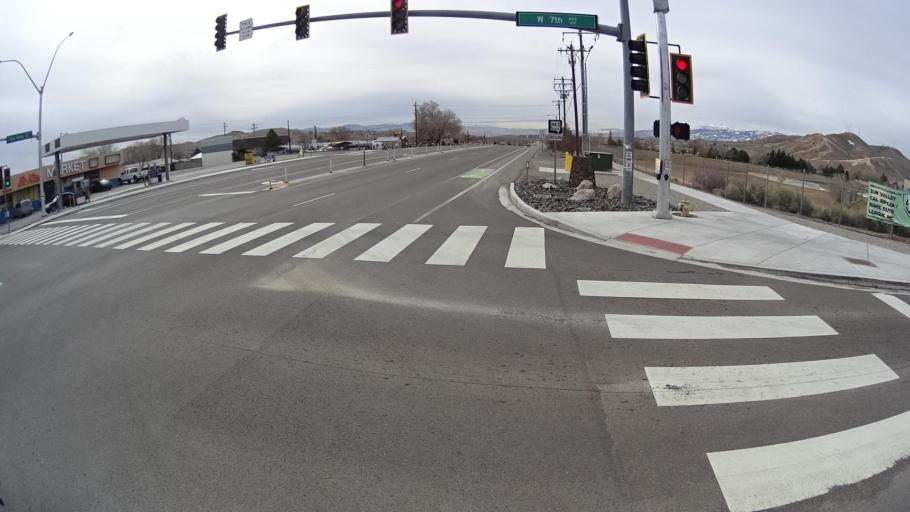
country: US
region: Nevada
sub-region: Washoe County
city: Sun Valley
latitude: 39.5999
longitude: -119.7809
